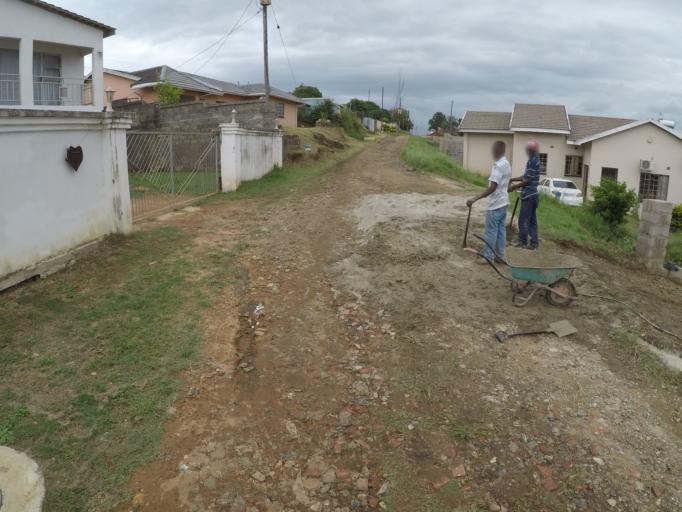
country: ZA
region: KwaZulu-Natal
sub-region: uThungulu District Municipality
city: Empangeni
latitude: -28.7843
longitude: 31.8580
